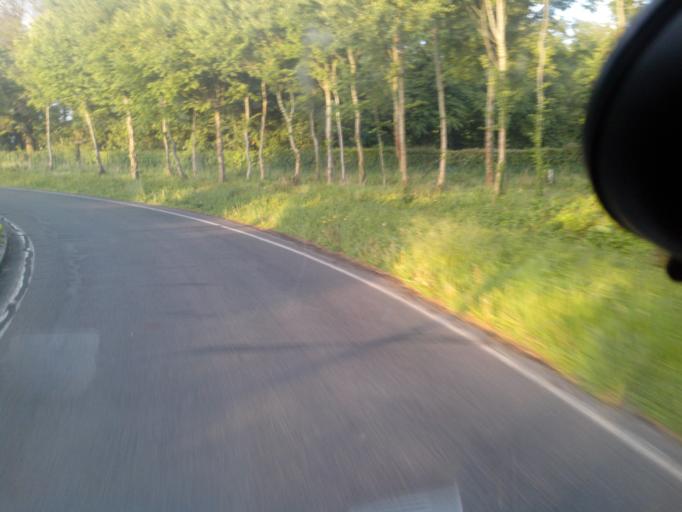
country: FR
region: Picardie
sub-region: Departement de la Somme
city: Oisemont
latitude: 50.0434
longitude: 1.7631
